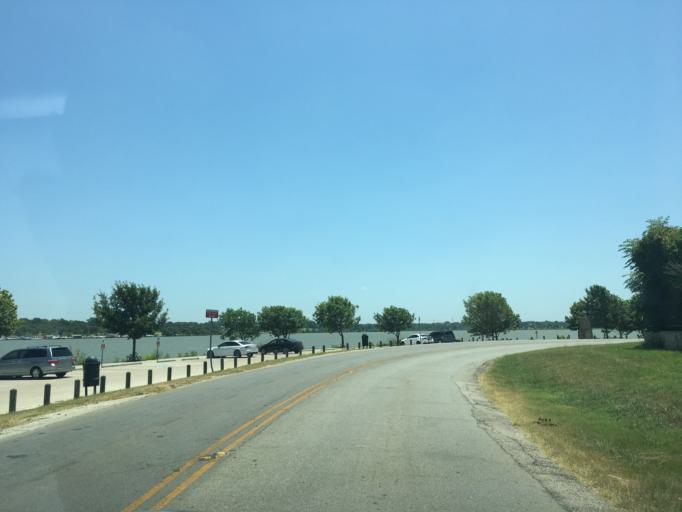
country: US
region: Texas
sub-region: Dallas County
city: Highland Park
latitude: 32.8465
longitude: -96.7281
